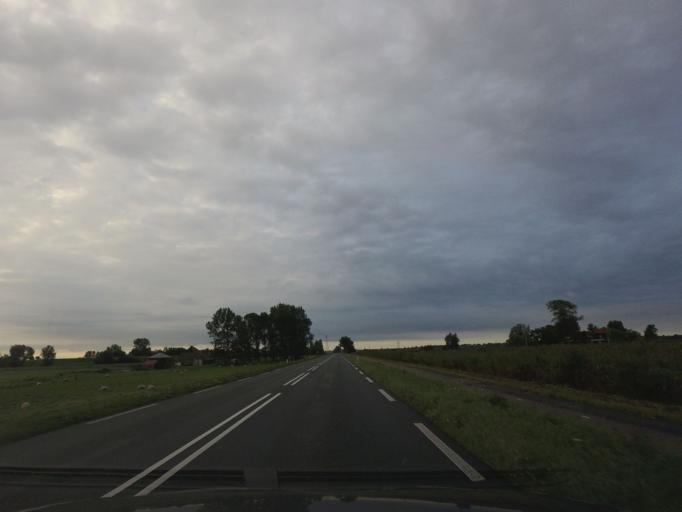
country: NL
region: North Holland
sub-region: Gemeente Uitgeest
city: Uitgeest
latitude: 52.5367
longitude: 4.7780
